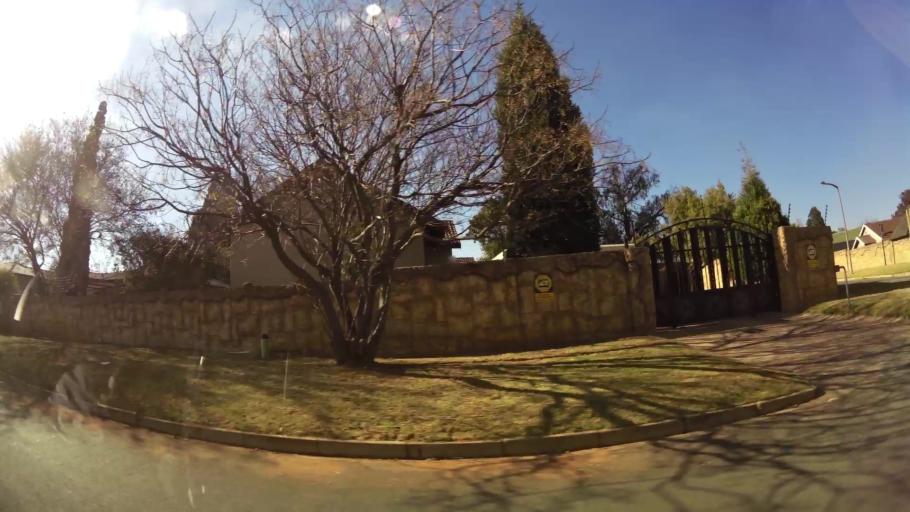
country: ZA
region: Gauteng
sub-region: City of Johannesburg Metropolitan Municipality
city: Roodepoort
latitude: -26.1433
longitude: 27.8219
